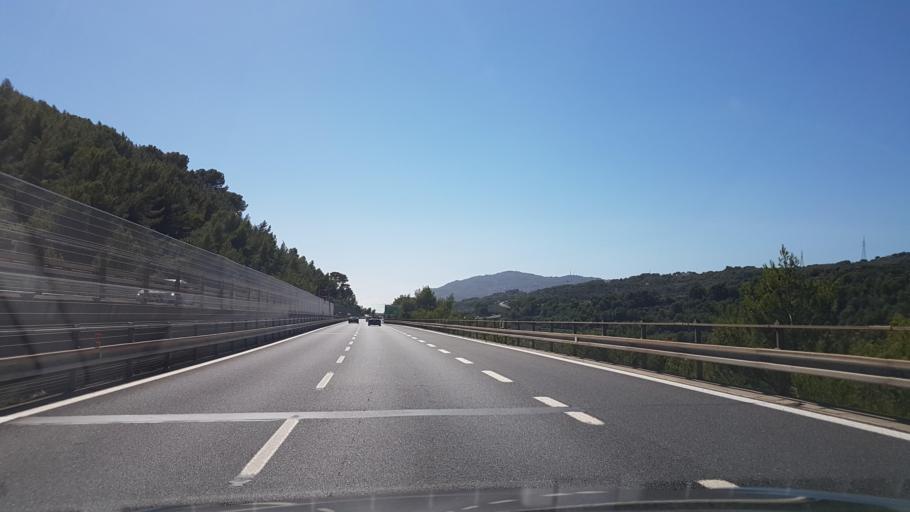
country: IT
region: Liguria
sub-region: Provincia di Imperia
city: Cervo
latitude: 43.9397
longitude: 8.1087
